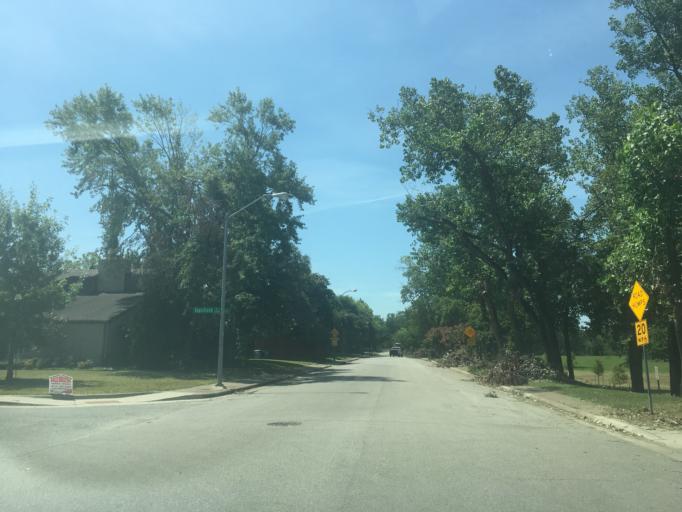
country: US
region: Texas
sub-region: Dallas County
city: University Park
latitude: 32.8745
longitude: -96.7400
